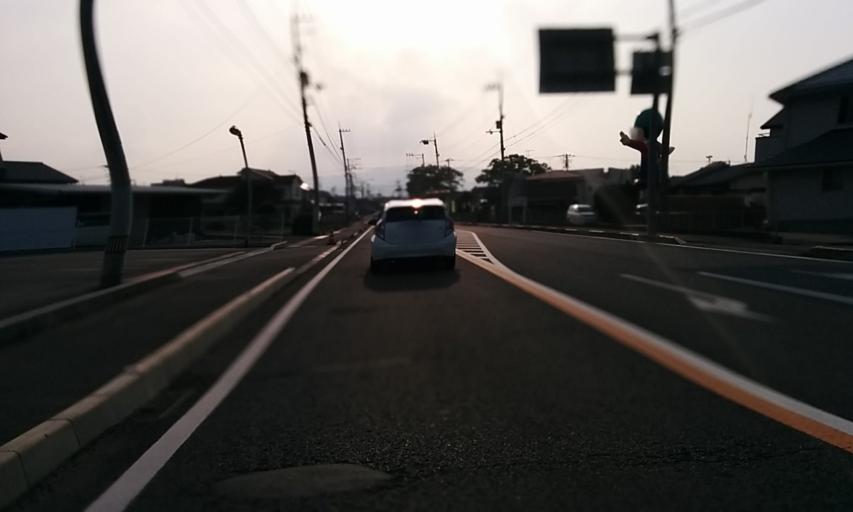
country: JP
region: Ehime
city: Saijo
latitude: 33.8954
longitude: 133.1321
